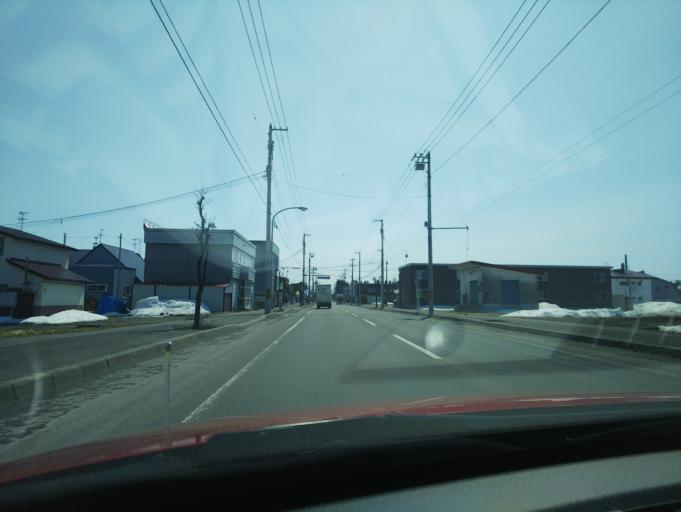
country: JP
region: Hokkaido
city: Nayoro
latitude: 44.3427
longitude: 142.4643
